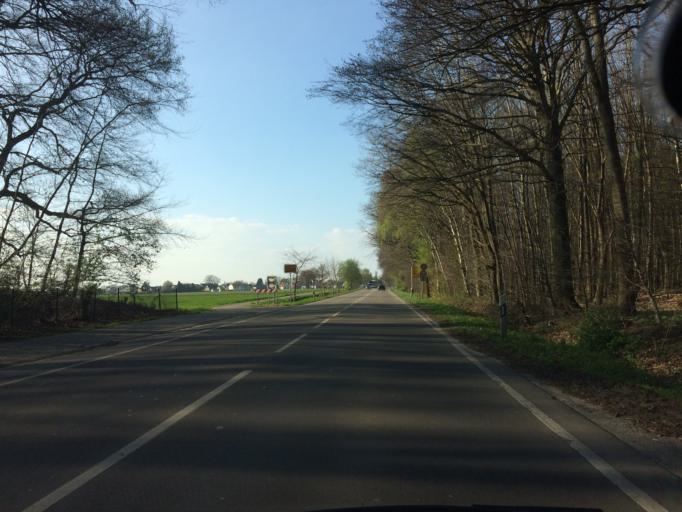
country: DE
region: North Rhine-Westphalia
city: Herten
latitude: 51.6185
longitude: 7.1128
